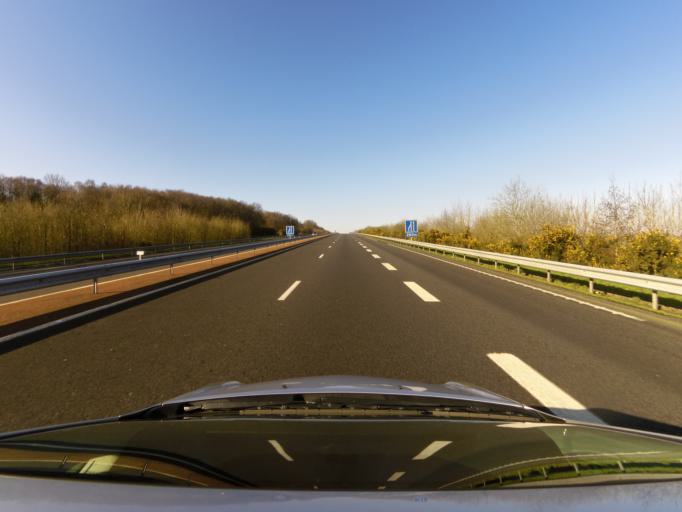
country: FR
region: Lower Normandy
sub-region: Departement de la Manche
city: Tessy-sur-Vire
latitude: 48.9188
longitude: -1.0865
